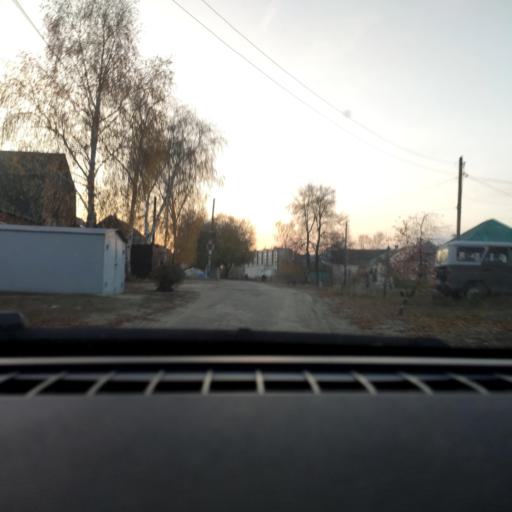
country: RU
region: Voronezj
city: Voronezh
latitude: 51.7038
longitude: 39.2666
